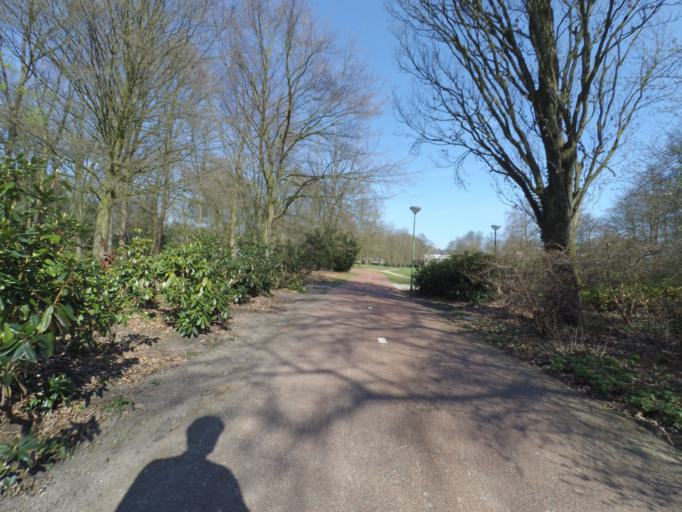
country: NL
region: Utrecht
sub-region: Gemeente Utrechtse Heuvelrug
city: Driebergen-Rijsenburg
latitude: 52.0525
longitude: 5.2773
